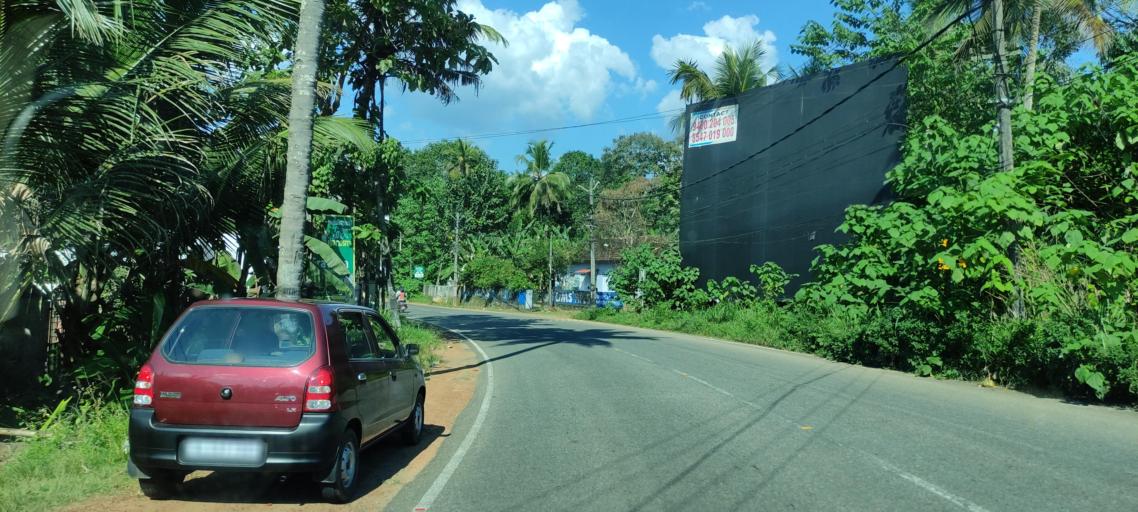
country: IN
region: Kerala
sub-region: Pattanamtitta
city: Pathanamthitta
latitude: 9.2325
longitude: 76.7548
